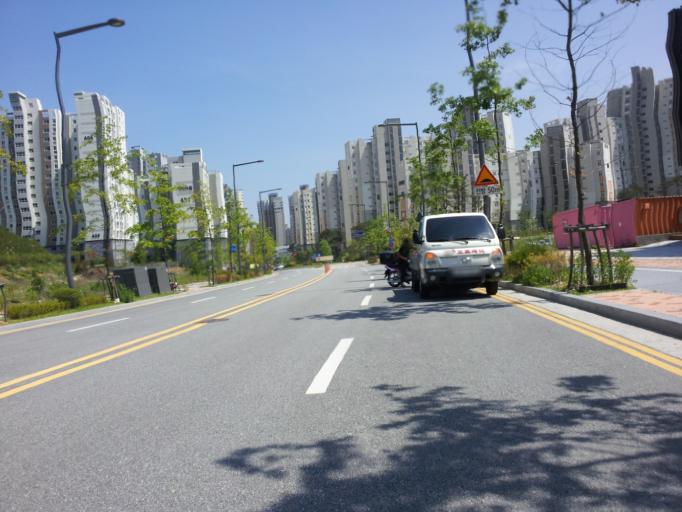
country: KR
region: Chungcheongnam-do
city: Gongju
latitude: 36.5085
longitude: 127.2347
